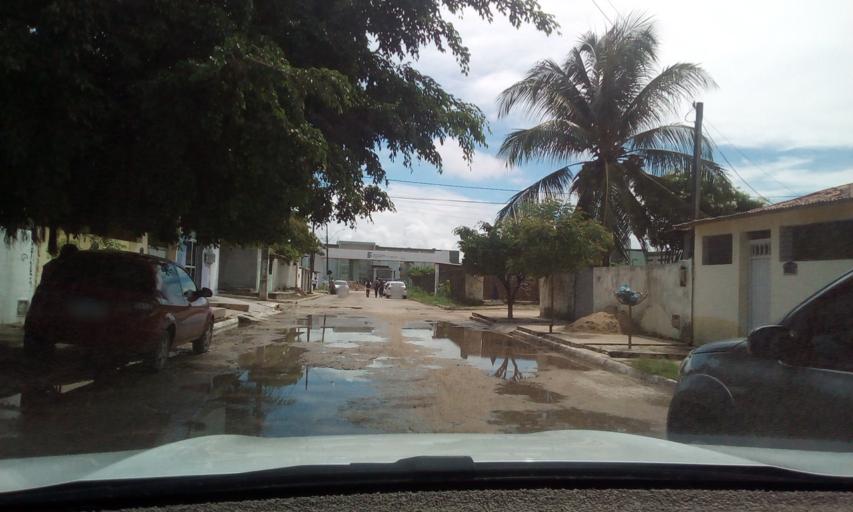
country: BR
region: Paraiba
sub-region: Cabedelo
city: Cabedelo
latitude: -7.0051
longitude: -34.8326
